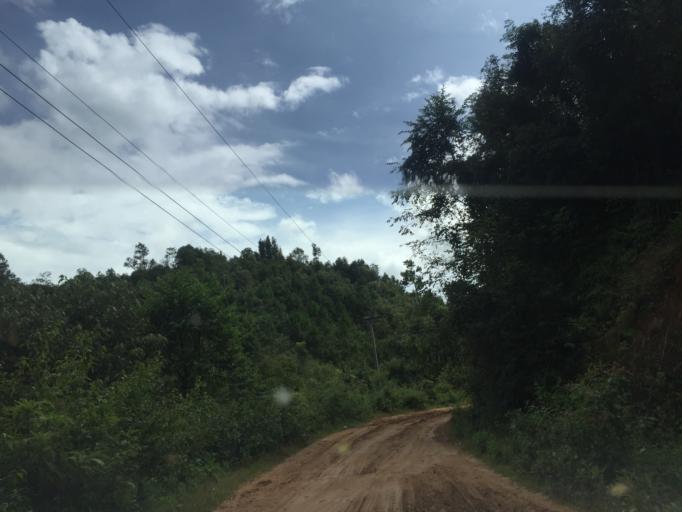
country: LA
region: Xiangkhoang
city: Muang Phonsavan
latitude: 19.3284
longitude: 103.4733
